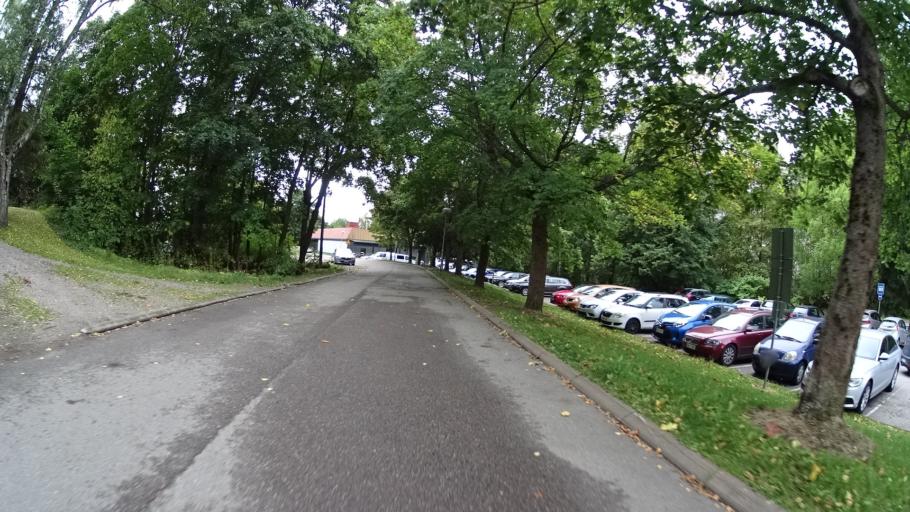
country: FI
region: Uusimaa
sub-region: Helsinki
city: Kauniainen
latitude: 60.2284
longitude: 24.7418
